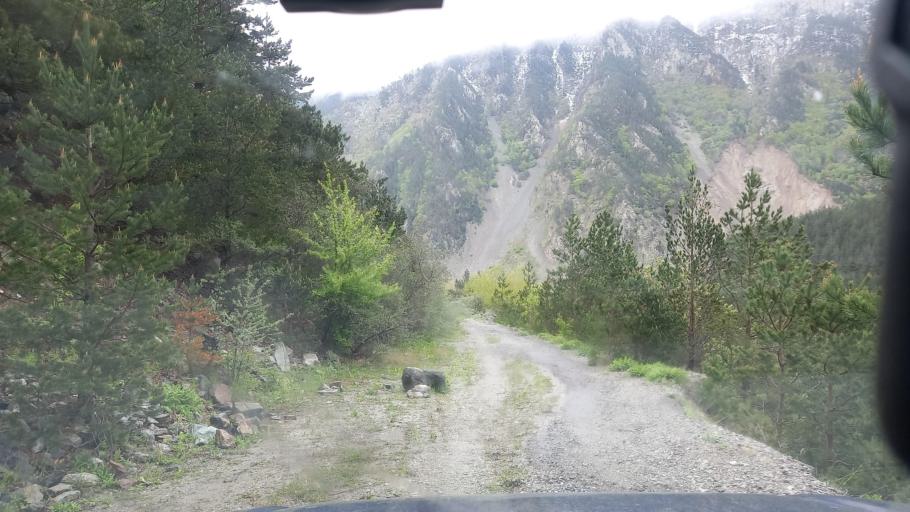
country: RU
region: North Ossetia
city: Mizur
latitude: 42.7917
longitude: 43.9963
